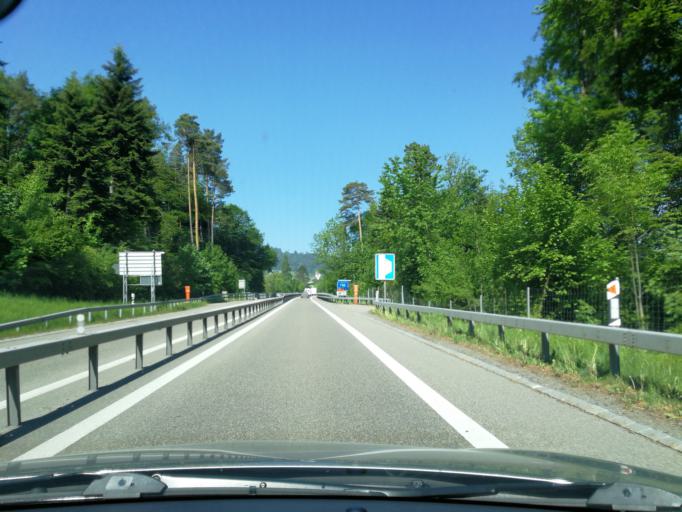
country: CH
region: Zurich
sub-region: Bezirk Uster
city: Egg
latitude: 47.2983
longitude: 8.7045
